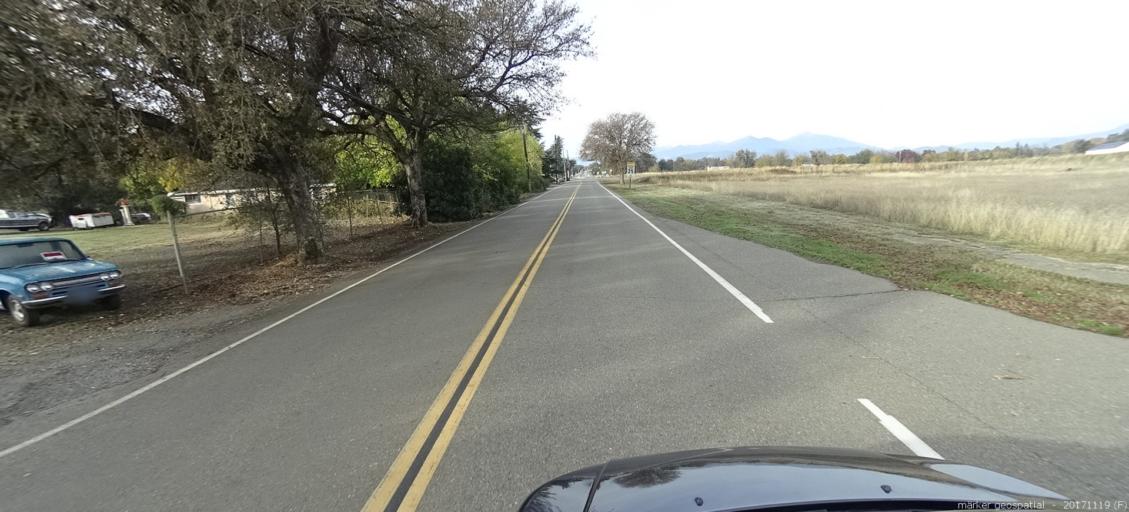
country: US
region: California
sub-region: Shasta County
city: Anderson
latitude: 40.5056
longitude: -122.3289
